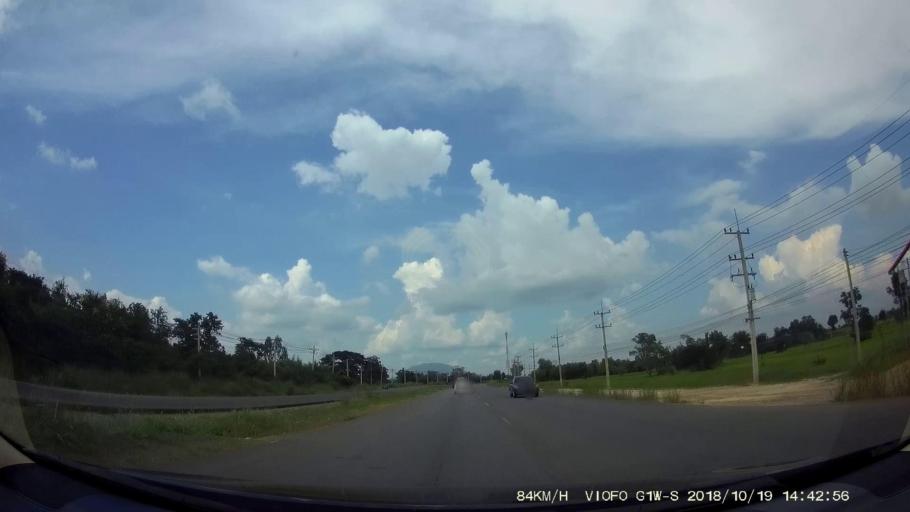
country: TH
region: Chaiyaphum
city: Phu Khiao
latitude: 16.2744
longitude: 102.2044
